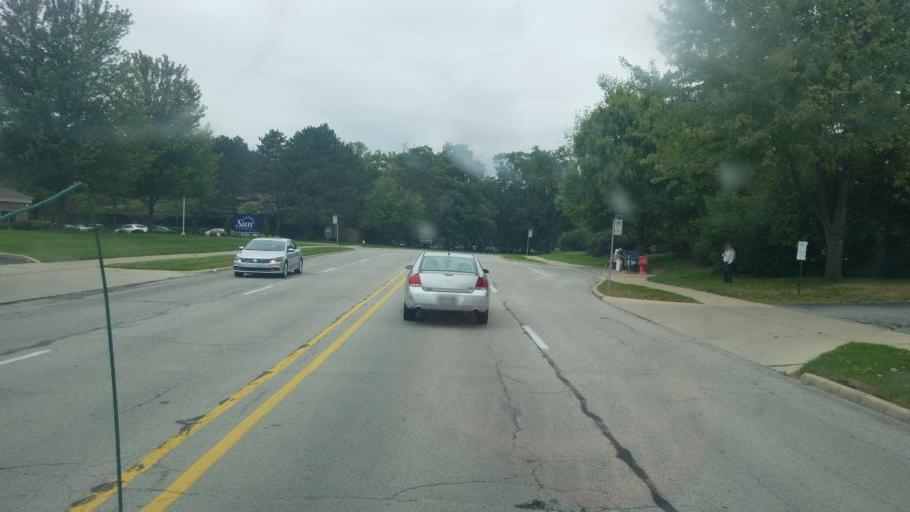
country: US
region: Ohio
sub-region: Lucas County
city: Ottawa Hills
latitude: 41.6805
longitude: -83.6287
